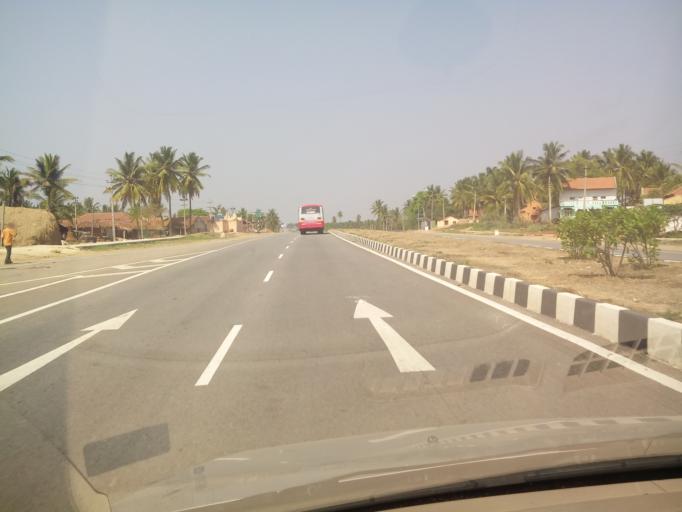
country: IN
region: Karnataka
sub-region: Hassan
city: Channarayapatna
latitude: 12.9093
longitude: 76.4404
